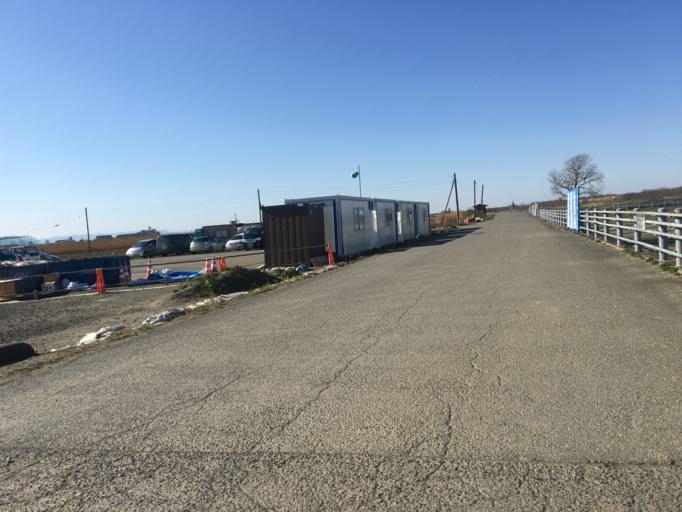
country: JP
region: Saitama
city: Shiki
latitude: 35.8403
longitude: 139.6032
